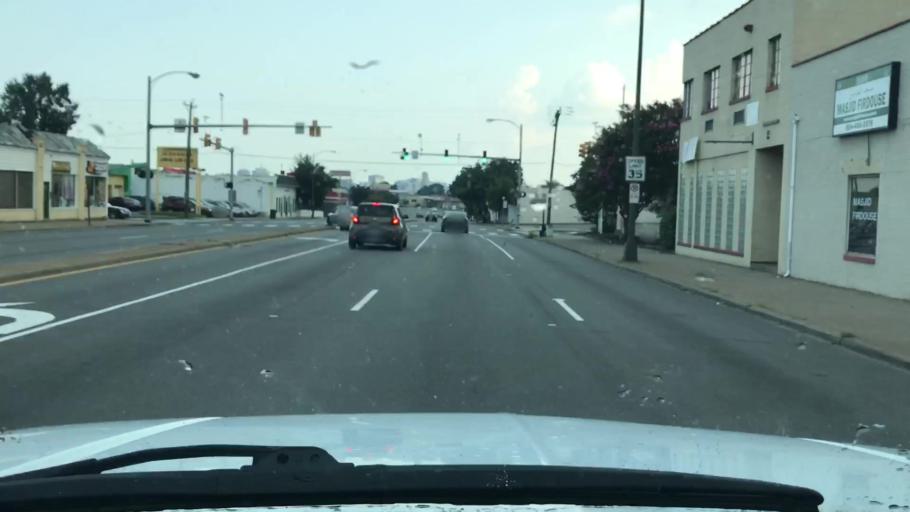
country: US
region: Virginia
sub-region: City of Richmond
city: Richmond
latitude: 37.5662
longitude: -77.4443
